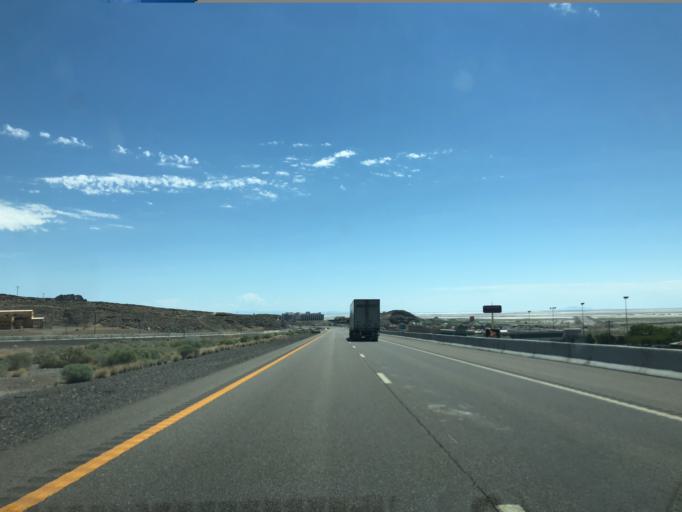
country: US
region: Nevada
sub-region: Elko County
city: West Wendover
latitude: 40.7407
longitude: -114.0612
